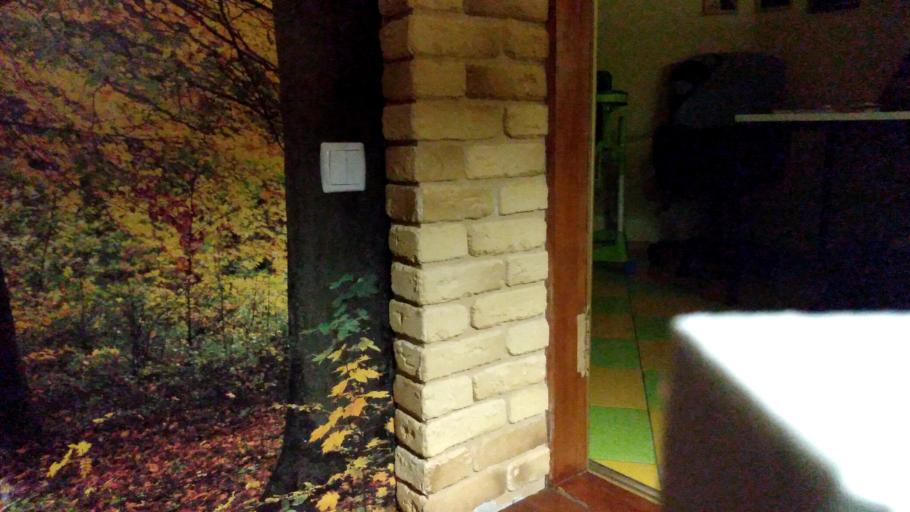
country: RU
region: Arkhangelskaya
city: Kargopol'
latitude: 61.3990
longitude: 37.8167
